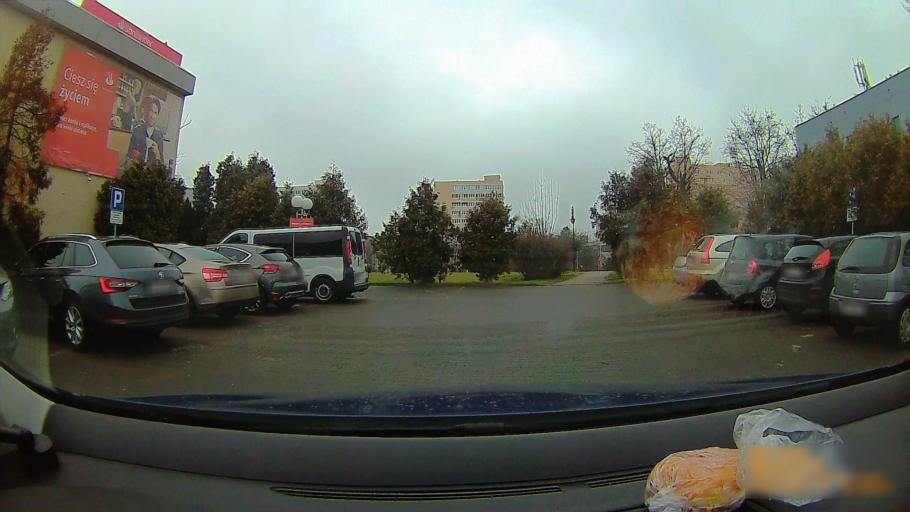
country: PL
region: Greater Poland Voivodeship
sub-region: Konin
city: Konin
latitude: 52.2274
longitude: 18.2521
